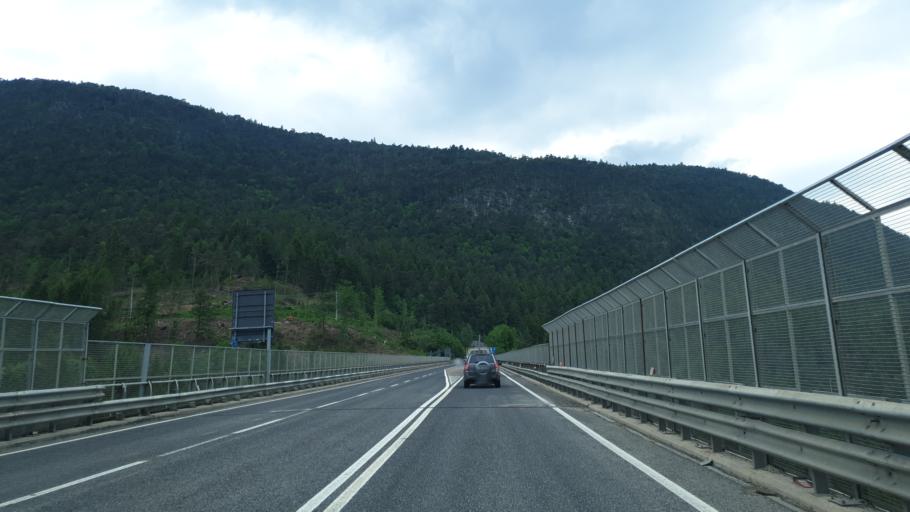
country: IT
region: Veneto
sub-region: Provincia di Belluno
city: Perarolo di Cadore
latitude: 46.4059
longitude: 12.3695
